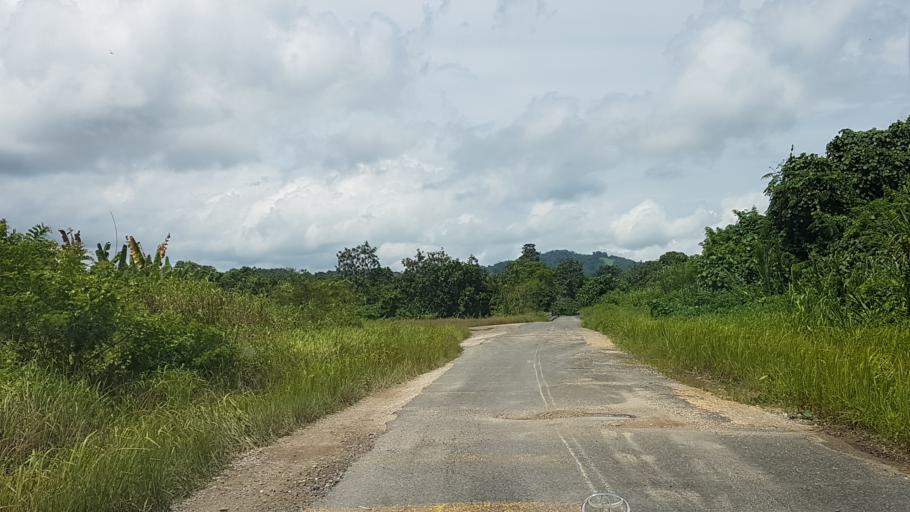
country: PG
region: Madang
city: Madang
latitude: -4.5380
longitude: 145.4820
